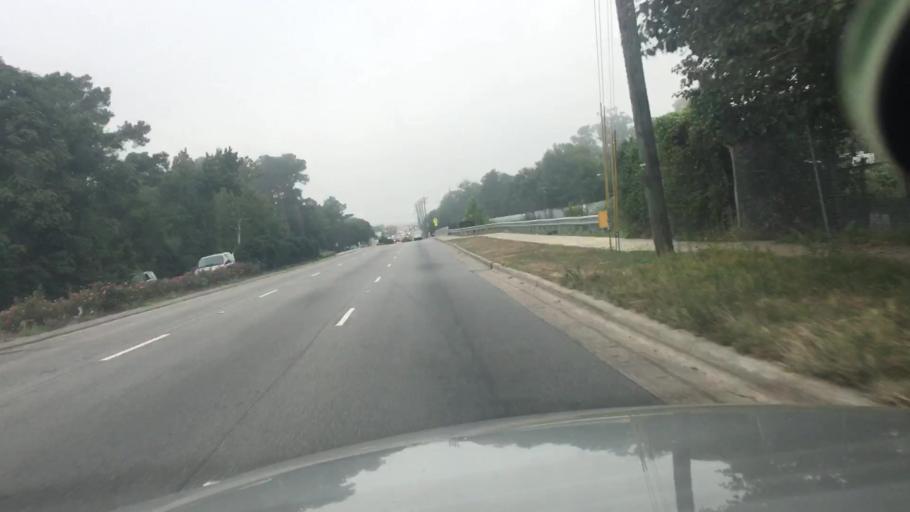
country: US
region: North Carolina
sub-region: Cumberland County
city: Fayetteville
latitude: 35.0549
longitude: -78.8702
